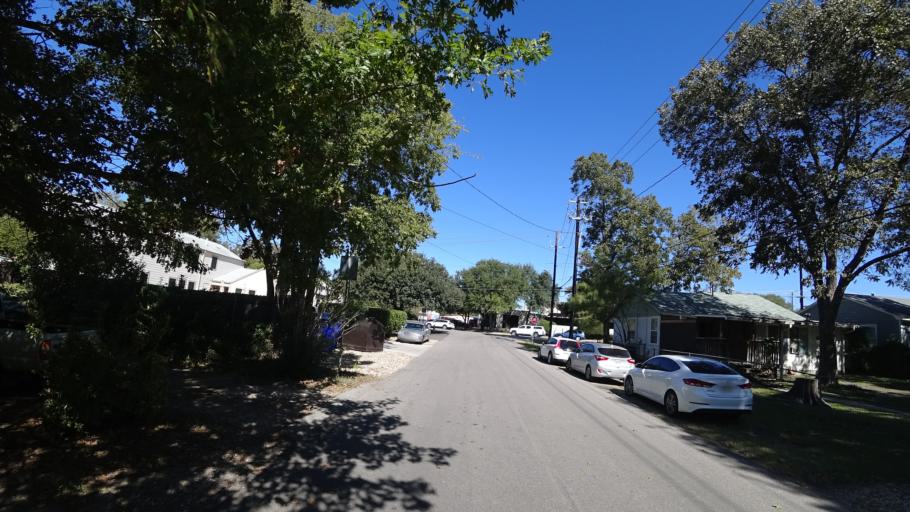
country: US
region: Texas
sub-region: Travis County
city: Austin
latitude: 30.3324
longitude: -97.7416
